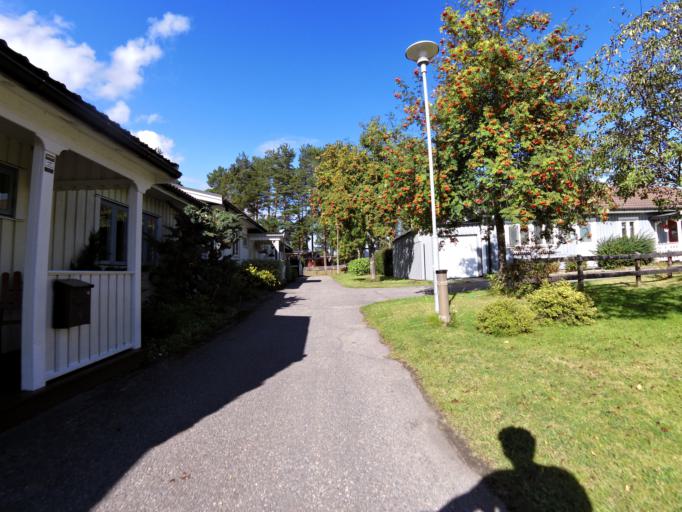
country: SE
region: Gaevleborg
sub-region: Gavle Kommun
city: Gavle
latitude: 60.6675
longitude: 17.2167
